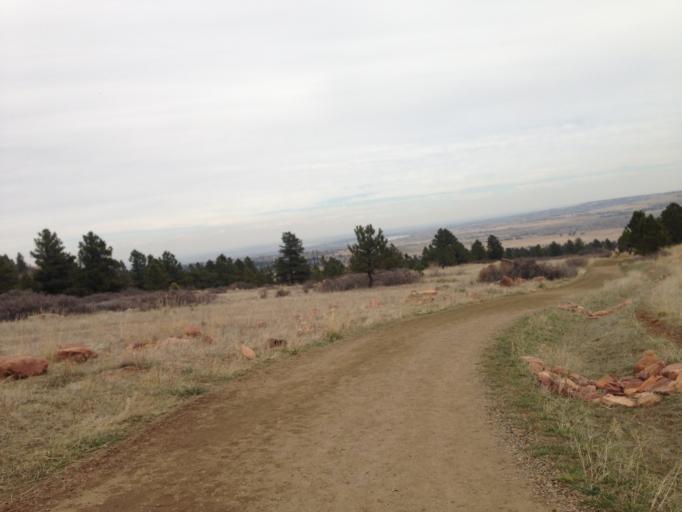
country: US
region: Colorado
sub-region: Boulder County
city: Boulder
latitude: 39.9457
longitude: -105.2702
